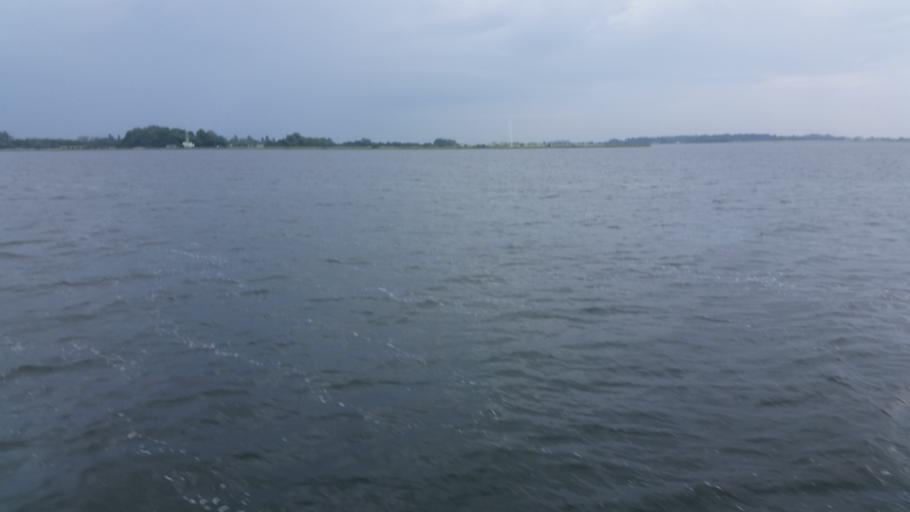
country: DE
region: Mecklenburg-Vorpommern
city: Hiddensee
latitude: 54.5423
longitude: 13.1312
